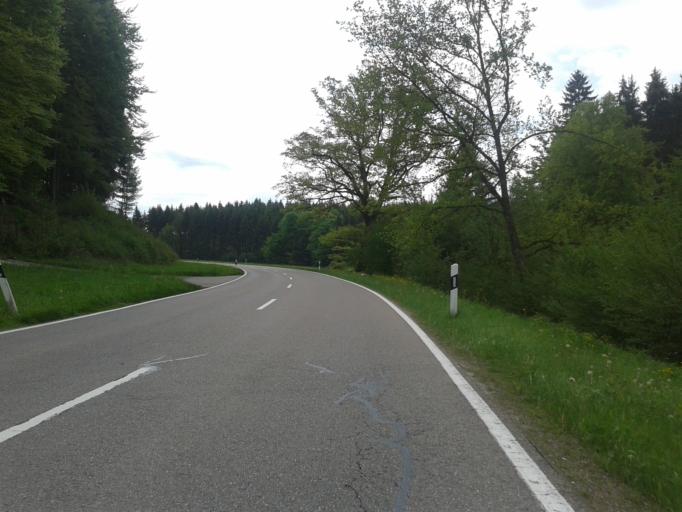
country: DE
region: Baden-Wuerttemberg
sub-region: Tuebingen Region
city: Erbach
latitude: 48.3554
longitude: 9.8457
